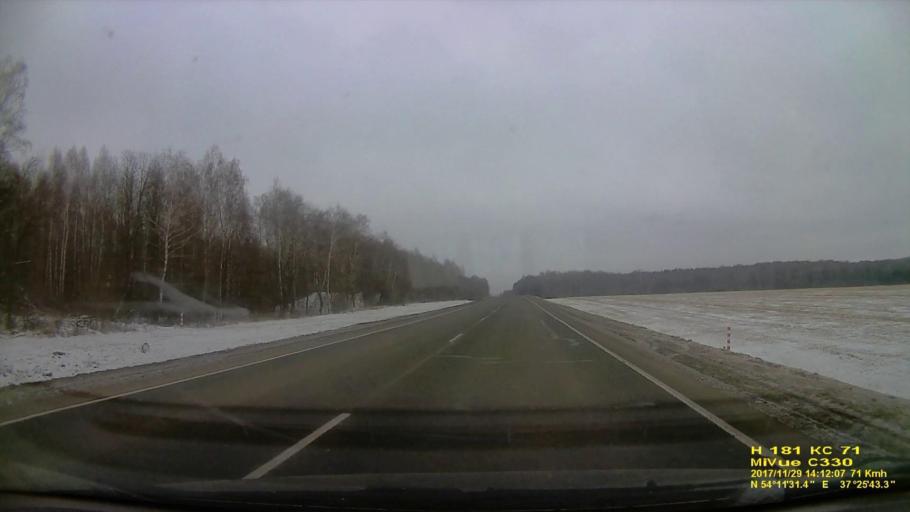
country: RU
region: Tula
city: Barsuki
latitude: 54.1919
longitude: 37.4289
